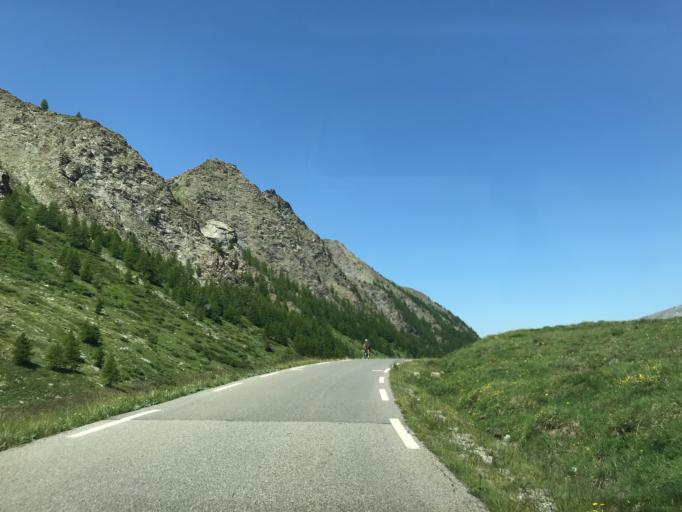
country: IT
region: Piedmont
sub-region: Provincia di Cuneo
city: Pontechianale
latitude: 44.6999
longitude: 6.9421
